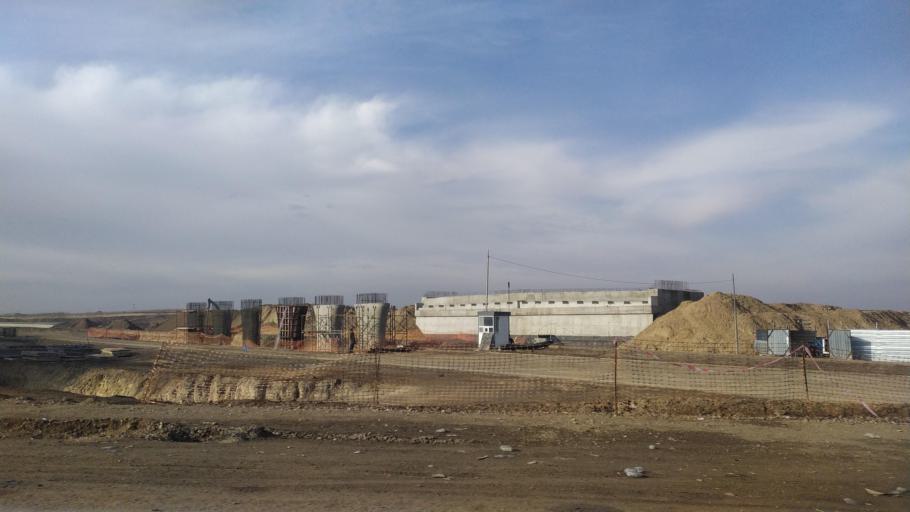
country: KZ
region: Almaty Oblysy
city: Burunday
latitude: 43.2249
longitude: 76.7299
